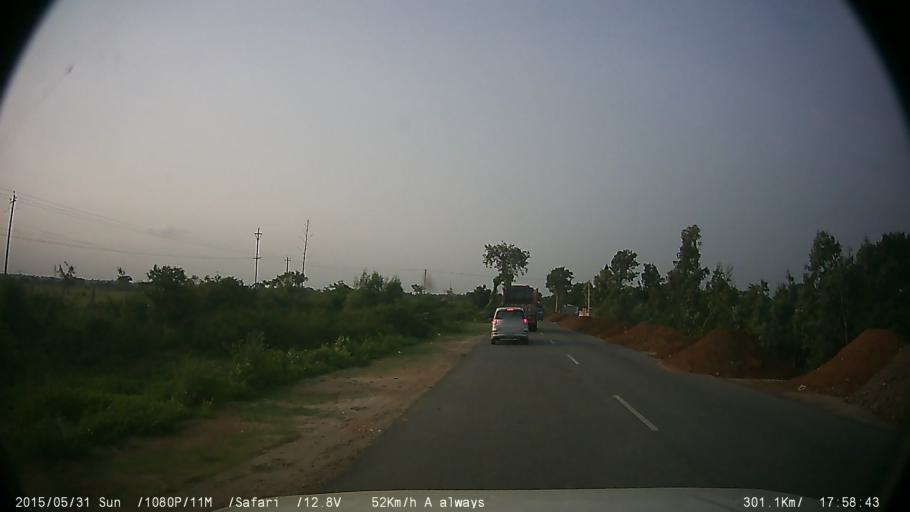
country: IN
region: Karnataka
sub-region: Mysore
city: Nanjangud
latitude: 12.0113
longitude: 76.6697
